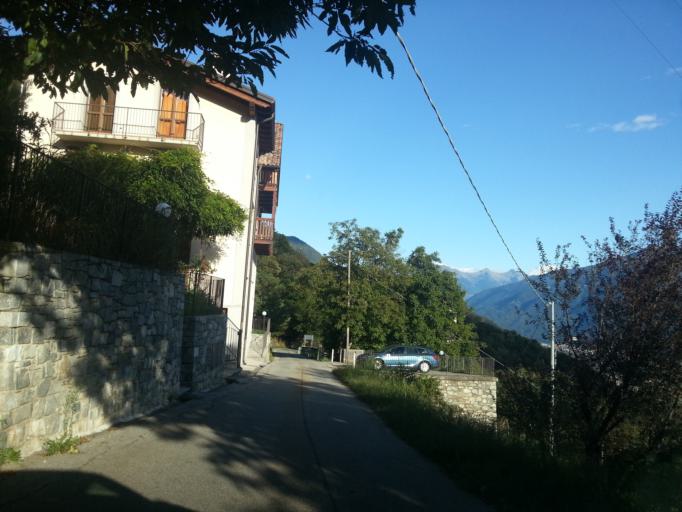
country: IT
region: Lombardy
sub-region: Provincia di Como
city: Sorico
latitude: 46.1833
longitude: 9.3855
